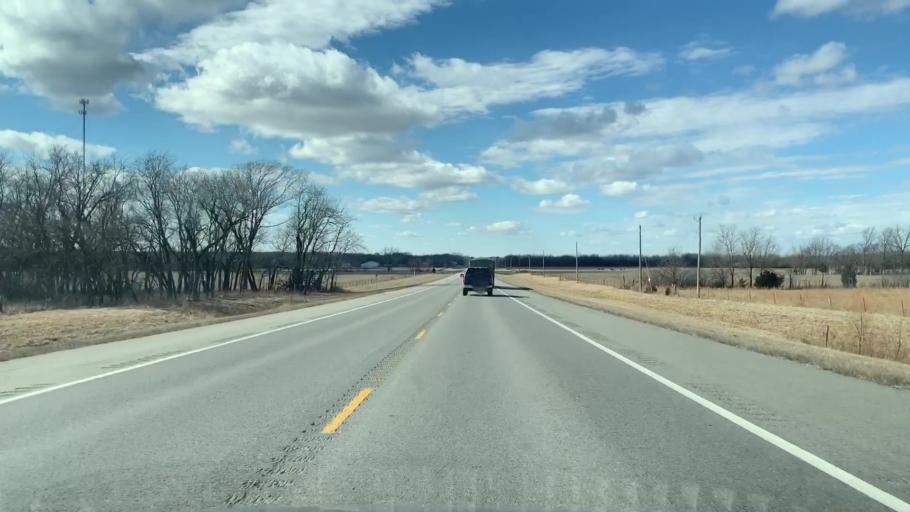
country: US
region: Kansas
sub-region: Cherokee County
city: Columbus
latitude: 37.3400
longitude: -94.9127
